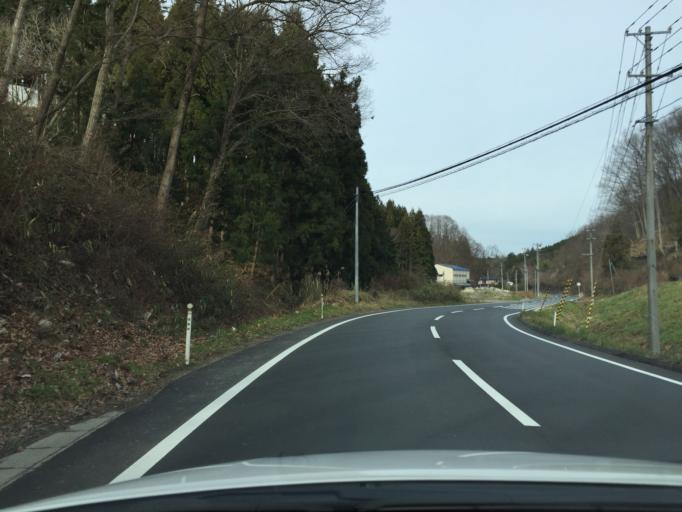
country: JP
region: Fukushima
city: Ishikawa
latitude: 37.2329
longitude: 140.6292
